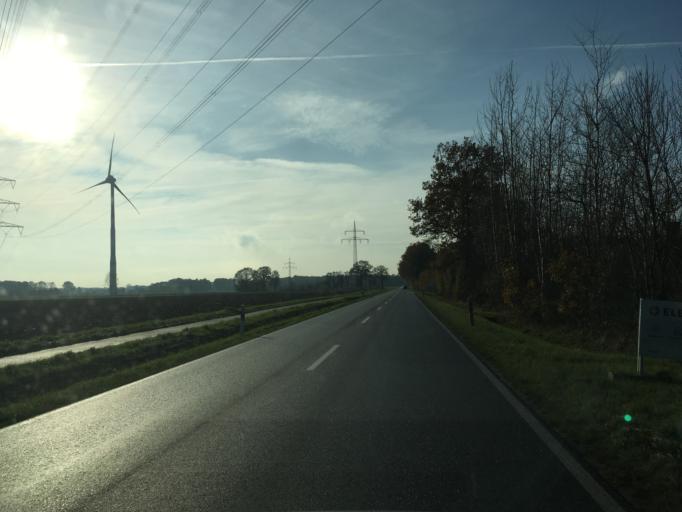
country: DE
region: North Rhine-Westphalia
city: Stadtlohn
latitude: 52.0343
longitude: 6.9614
